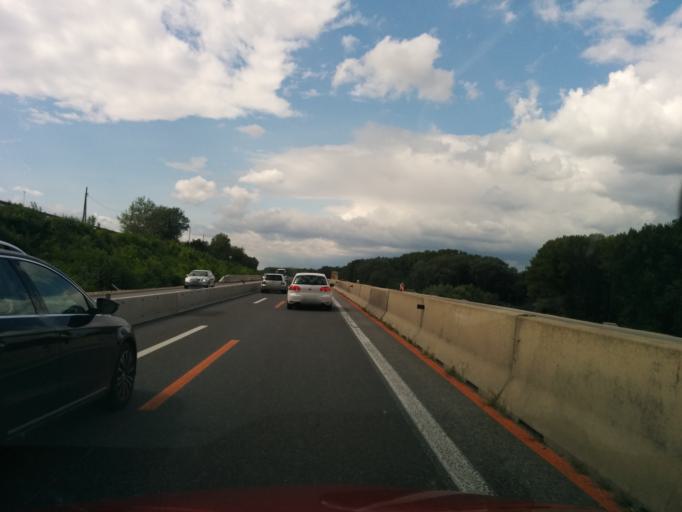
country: AT
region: Lower Austria
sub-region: Politischer Bezirk Wien-Umgebung
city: Fischamend Dorf
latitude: 48.1263
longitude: 16.5918
